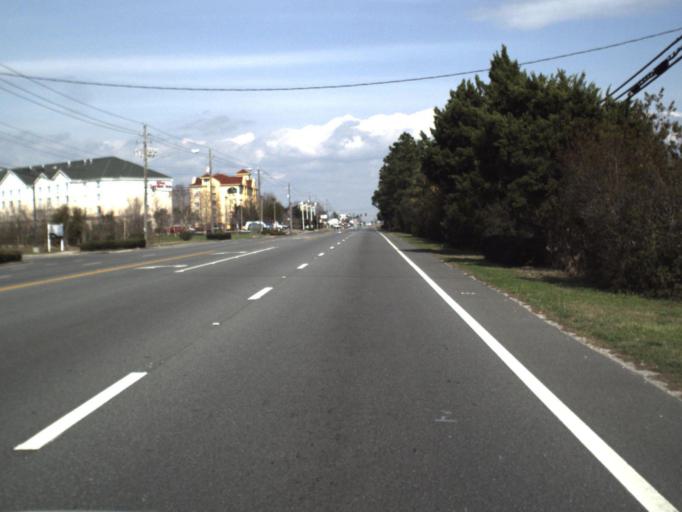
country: US
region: Florida
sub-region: Bay County
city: Hiland Park
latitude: 30.1865
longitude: -85.6449
